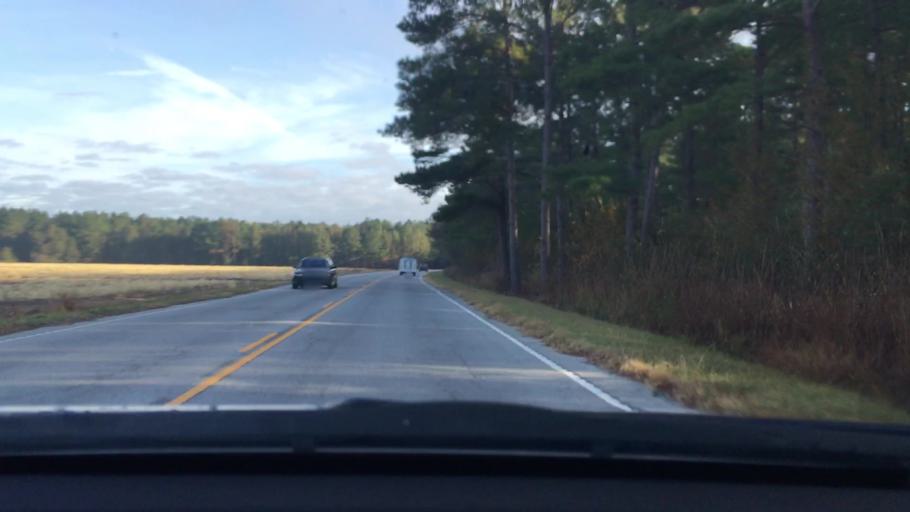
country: US
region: South Carolina
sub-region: Sumter County
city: East Sumter
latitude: 34.0288
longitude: -80.2740
